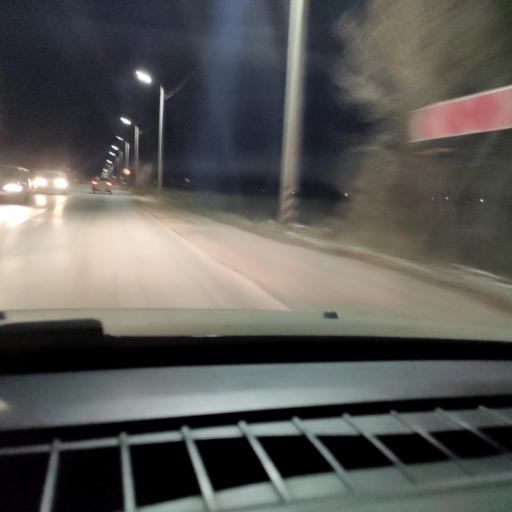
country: RU
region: Samara
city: Podstepki
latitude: 53.5221
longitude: 49.1765
